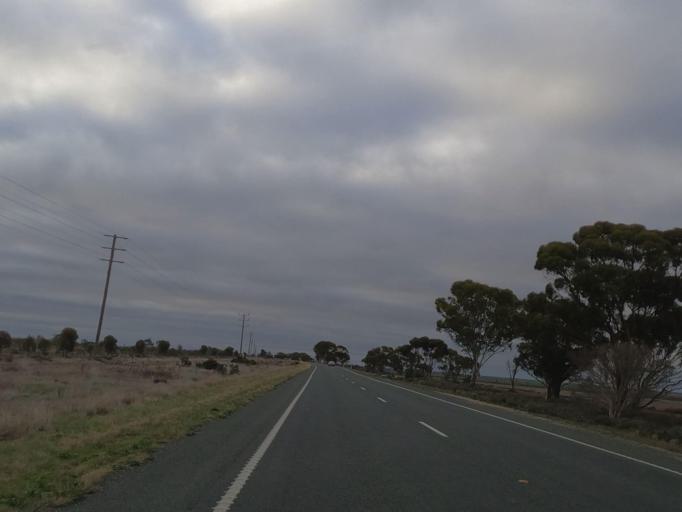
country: AU
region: Victoria
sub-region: Swan Hill
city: Swan Hill
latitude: -35.5771
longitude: 143.7882
